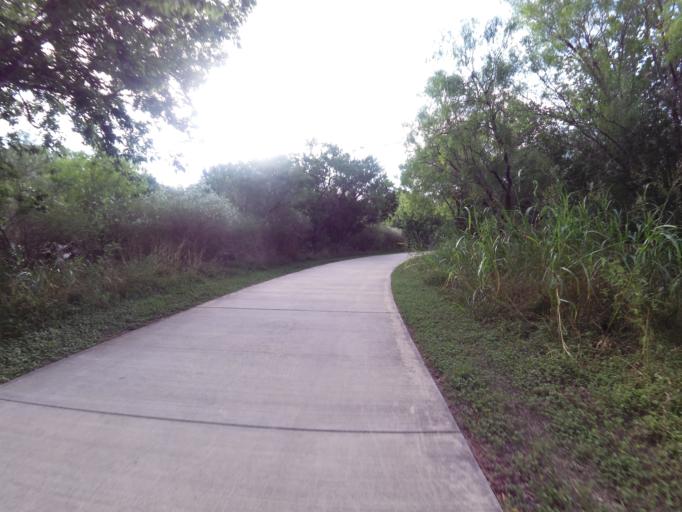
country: US
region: Texas
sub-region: Bexar County
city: Leon Valley
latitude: 29.4879
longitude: -98.6360
